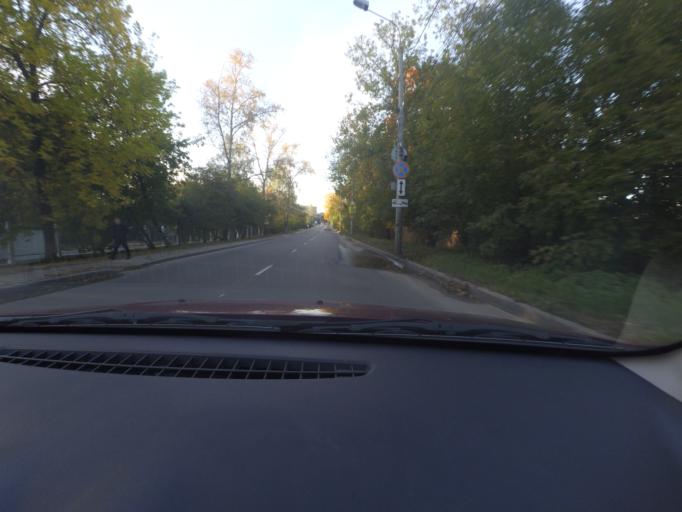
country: RU
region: Nizjnij Novgorod
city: Nizhniy Novgorod
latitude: 56.2725
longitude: 43.9921
